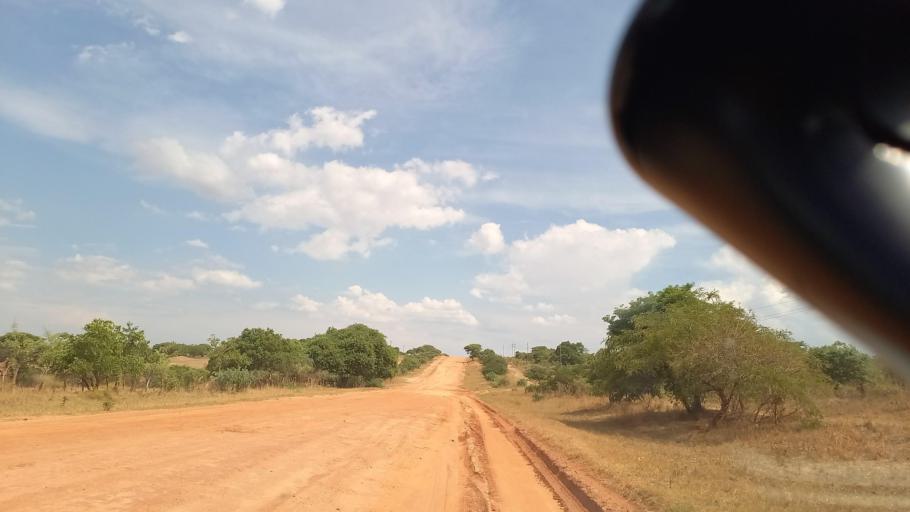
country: ZM
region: Lusaka
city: Kafue
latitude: -16.1272
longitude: 28.0448
